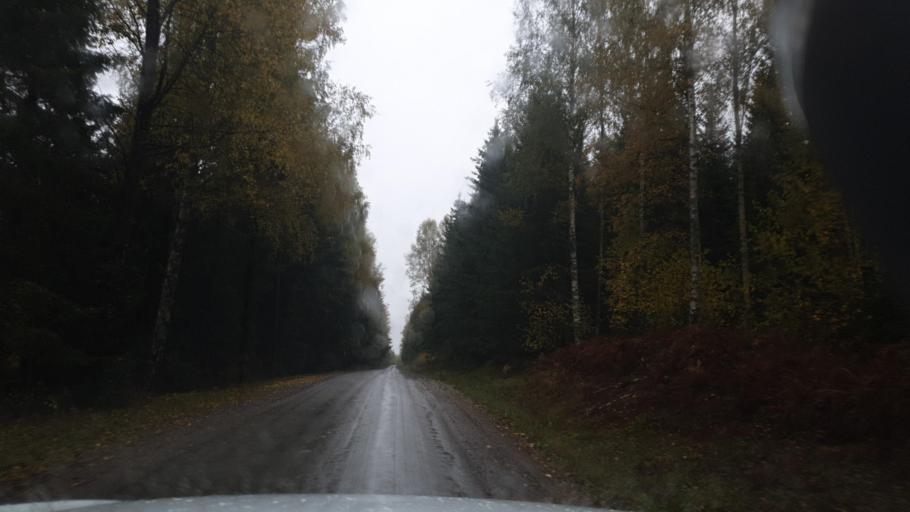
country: SE
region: Vaermland
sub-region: Eda Kommun
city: Amotfors
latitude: 59.7505
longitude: 12.2722
